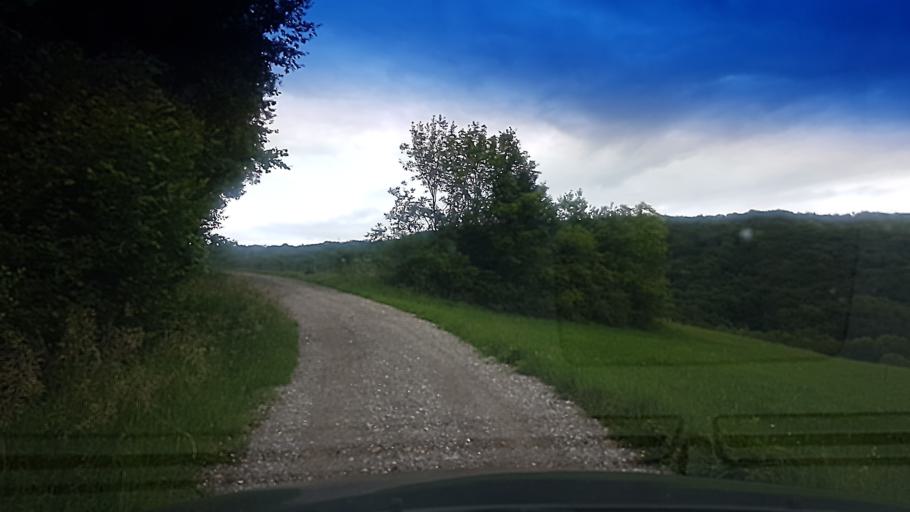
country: DE
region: Bavaria
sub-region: Upper Franconia
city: Buttenheim
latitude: 49.8311
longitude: 11.0533
